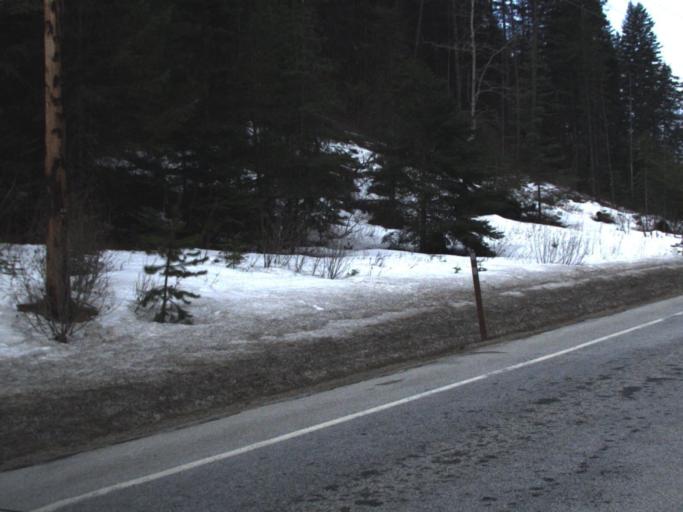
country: US
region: Washington
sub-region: Pend Oreille County
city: Newport
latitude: 48.2183
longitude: -117.0899
